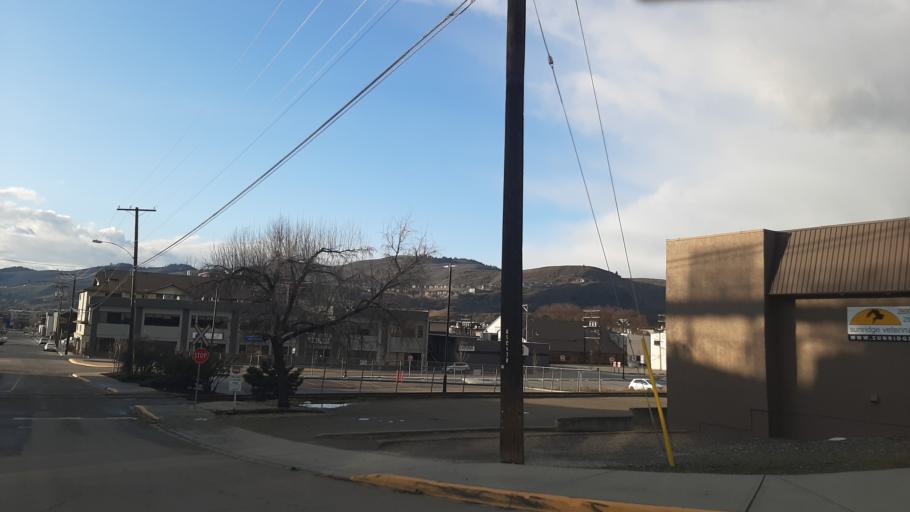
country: CA
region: British Columbia
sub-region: Regional District of North Okanagan
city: Vernon
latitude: 50.2622
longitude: -119.2680
